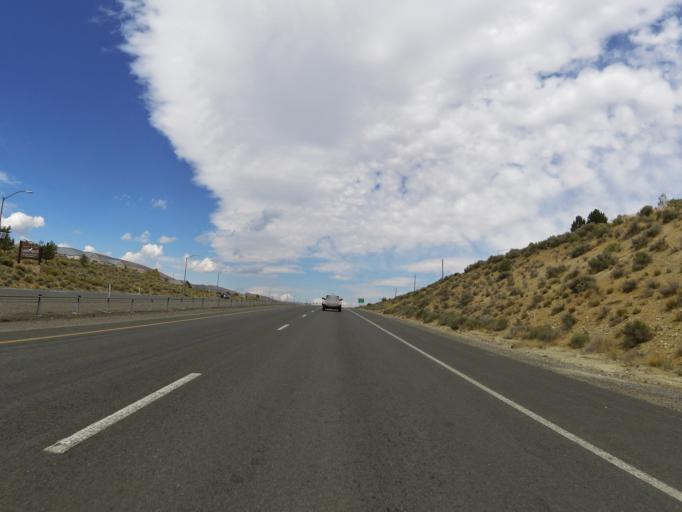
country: US
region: Nevada
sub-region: Douglas County
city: Indian Hills
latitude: 39.0970
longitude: -119.7748
